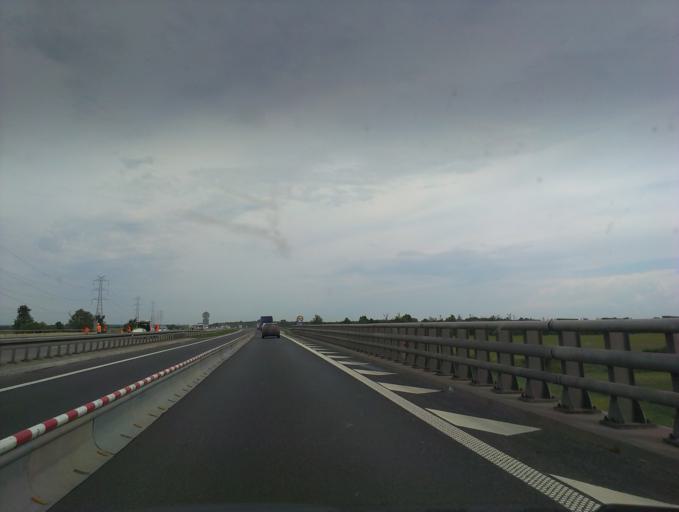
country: PL
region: Opole Voivodeship
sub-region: Powiat brzeski
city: Losiow
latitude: 50.7251
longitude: 17.5200
